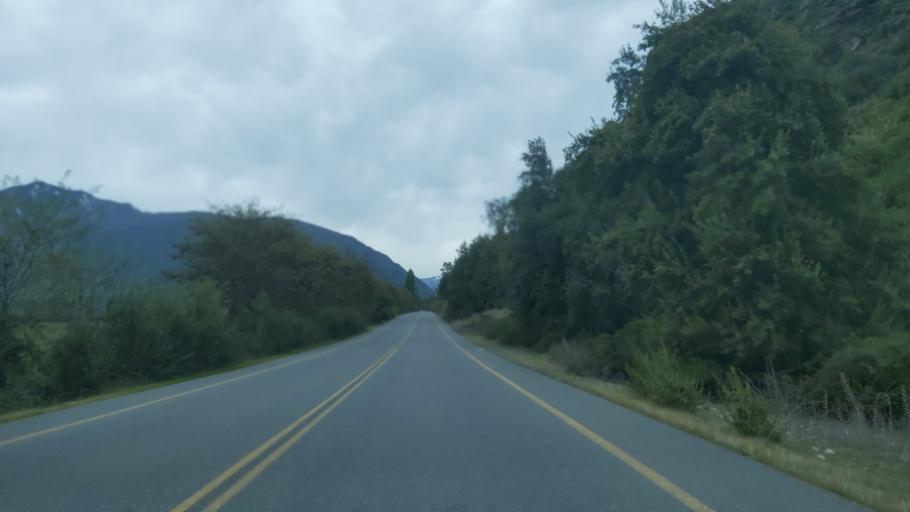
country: CL
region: Maule
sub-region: Provincia de Linares
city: Colbun
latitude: -35.8123
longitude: -70.8653
